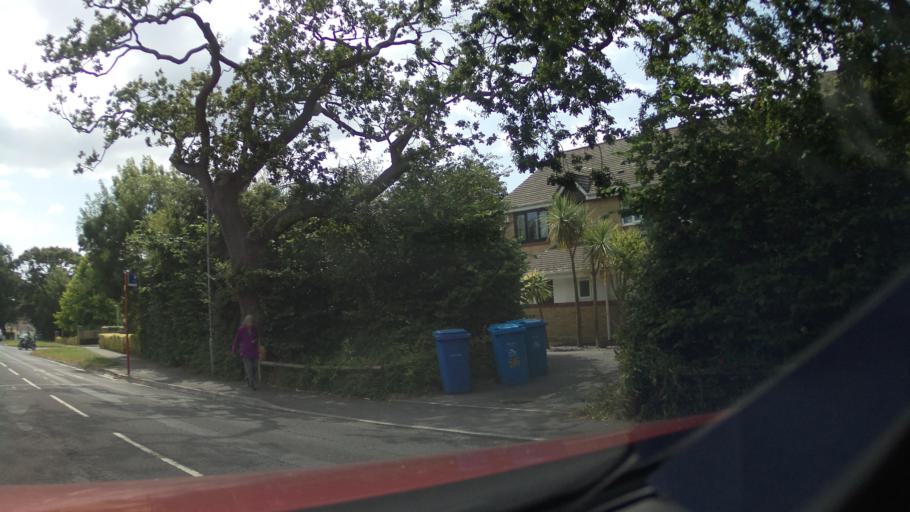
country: GB
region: England
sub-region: Poole
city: Poole
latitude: 50.7177
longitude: -2.0135
